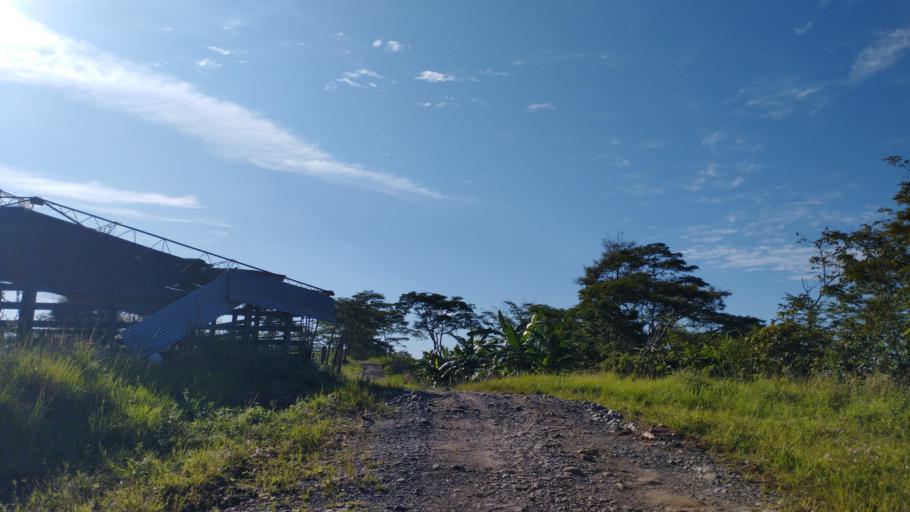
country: CO
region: Casanare
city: Sabanalarga
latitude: 4.7863
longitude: -73.0875
